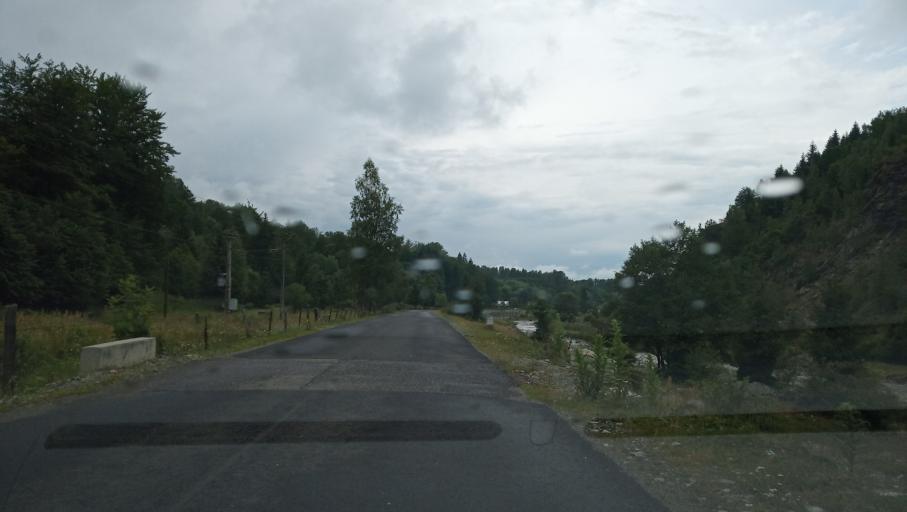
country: RO
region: Hunedoara
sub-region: Oras Petrila
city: Petrila
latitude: 45.4164
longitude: 23.4415
